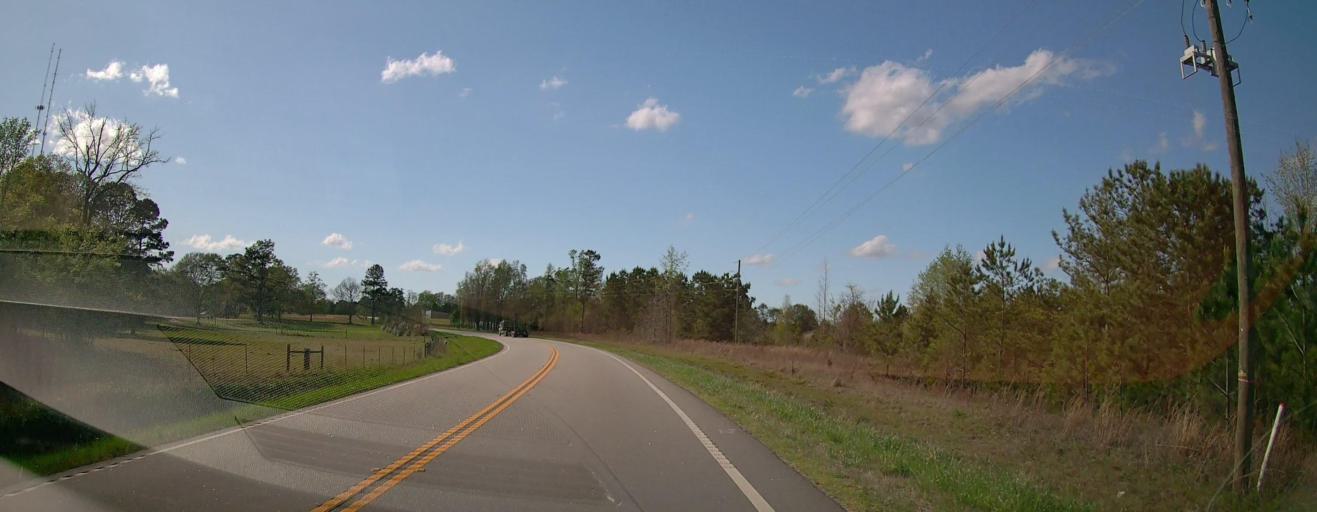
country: US
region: Georgia
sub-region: Baldwin County
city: Hardwick
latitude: 33.0776
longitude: -83.1407
